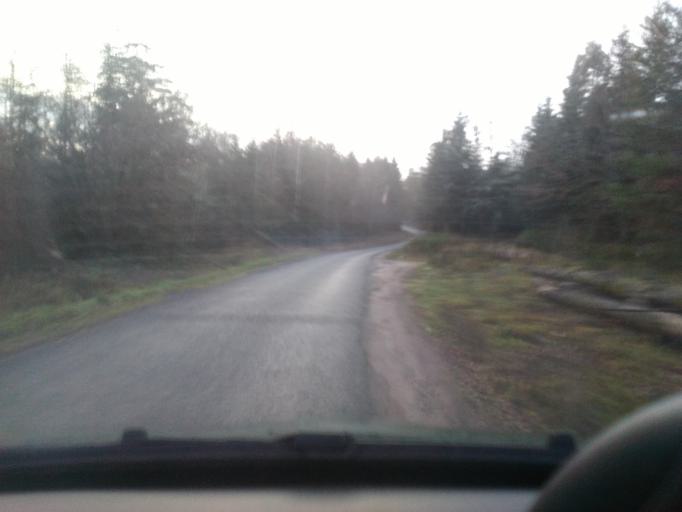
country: FR
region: Lorraine
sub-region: Departement des Vosges
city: Saint-Leonard
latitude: 48.2138
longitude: 6.9190
